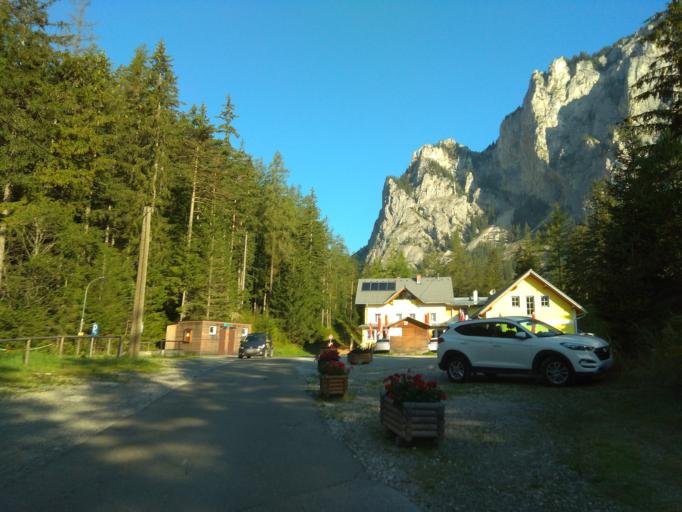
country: AT
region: Styria
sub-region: Politischer Bezirk Leoben
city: Vordernberg
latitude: 47.5395
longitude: 15.0577
